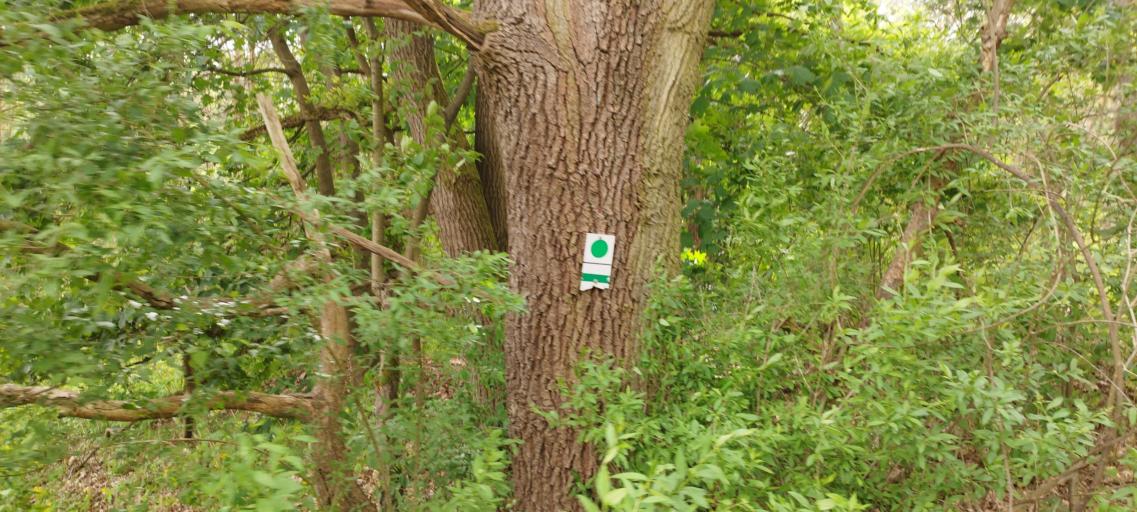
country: DE
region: Brandenburg
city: Furstenwalde
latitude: 52.3423
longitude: 14.0483
